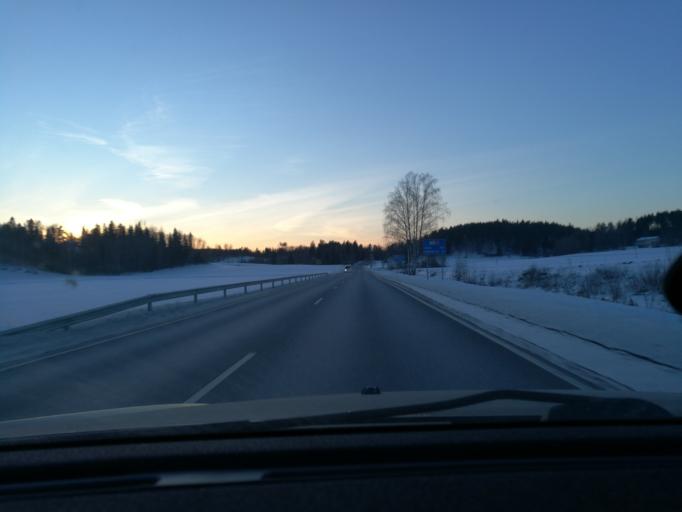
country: FI
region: Uusimaa
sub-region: Helsinki
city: Vihti
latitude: 60.4381
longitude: 24.3937
